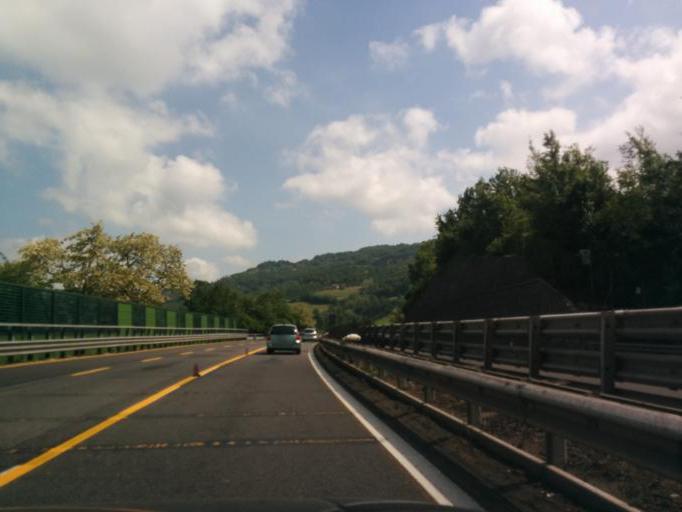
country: IT
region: Emilia-Romagna
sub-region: Provincia di Bologna
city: San Benedetto Val di Sambro
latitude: 44.1692
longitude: 11.2104
